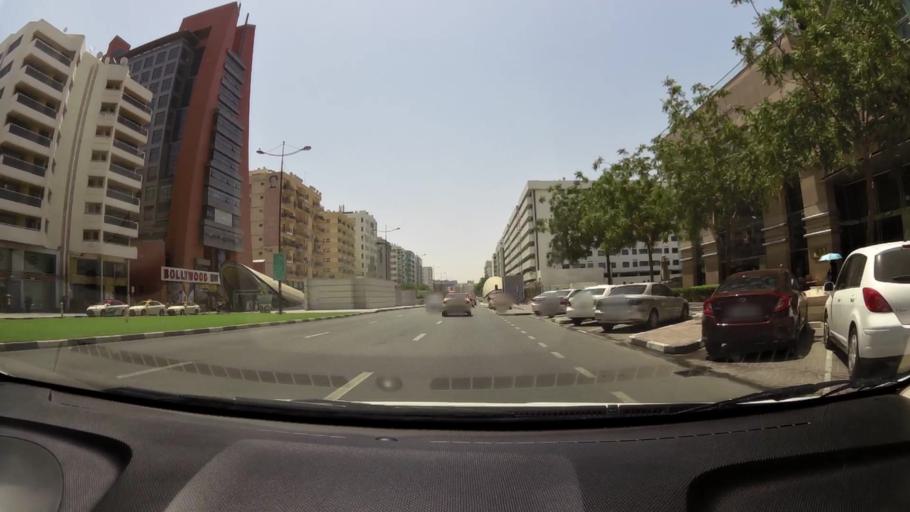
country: AE
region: Ash Shariqah
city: Sharjah
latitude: 25.2637
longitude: 55.3230
